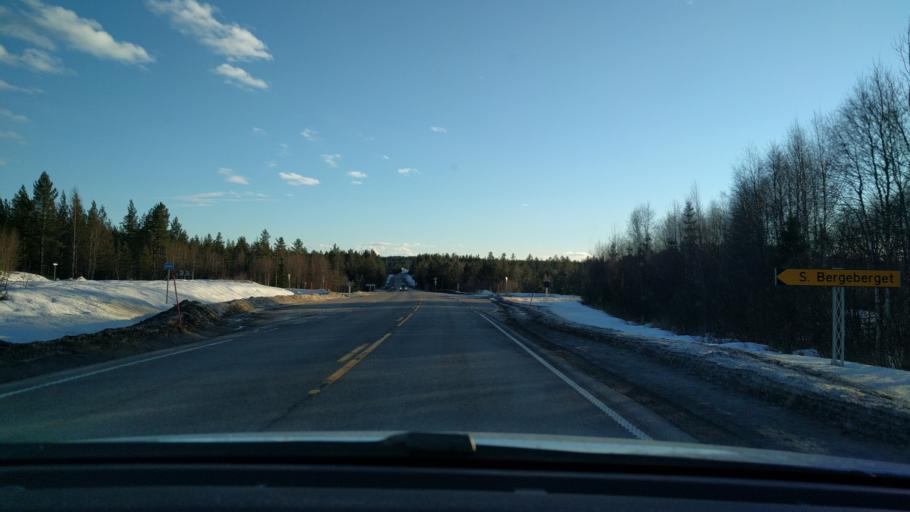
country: NO
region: Hedmark
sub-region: Elverum
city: Elverum
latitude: 60.9982
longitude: 11.7725
